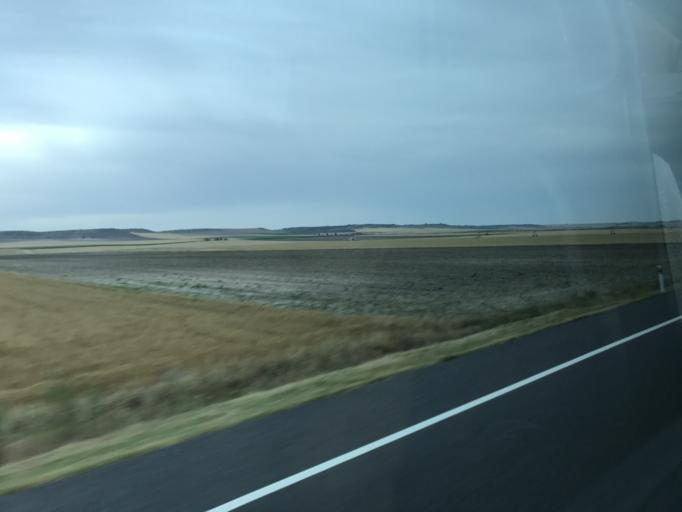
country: ES
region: Castille and Leon
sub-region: Provincia de Valladolid
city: Puras
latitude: 41.1673
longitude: -4.6556
